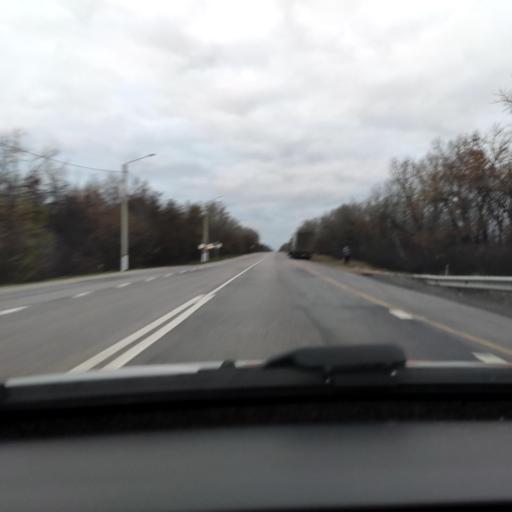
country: RU
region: Lipetsk
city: Khlevnoye
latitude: 52.2687
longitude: 39.1687
